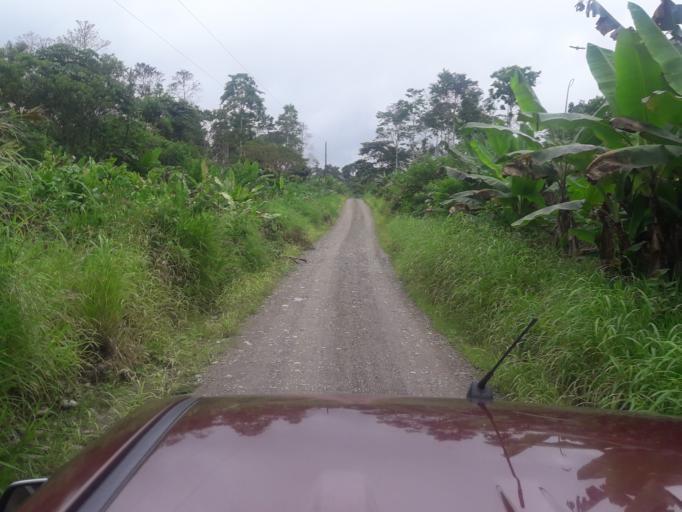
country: EC
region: Napo
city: Tena
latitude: -1.0260
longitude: -77.5998
